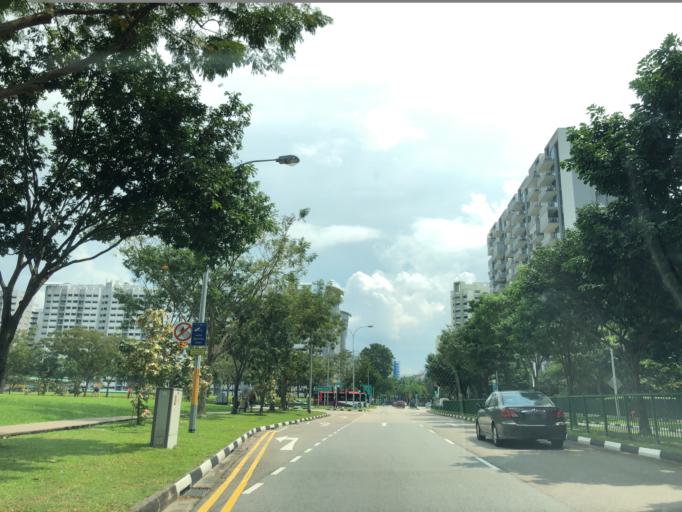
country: MY
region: Johor
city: Kampung Pasir Gudang Baru
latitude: 1.3905
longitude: 103.8953
